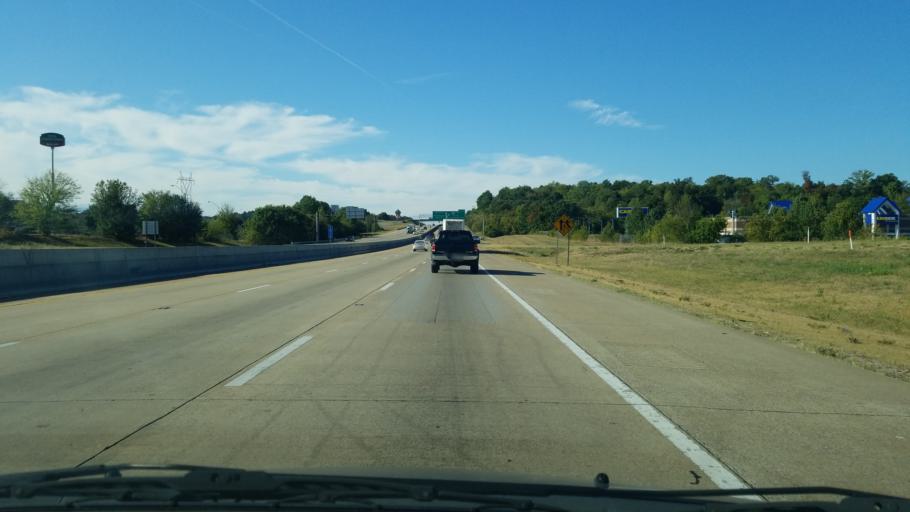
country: US
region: Tennessee
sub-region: Hamilton County
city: East Brainerd
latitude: 35.0412
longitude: -85.1566
